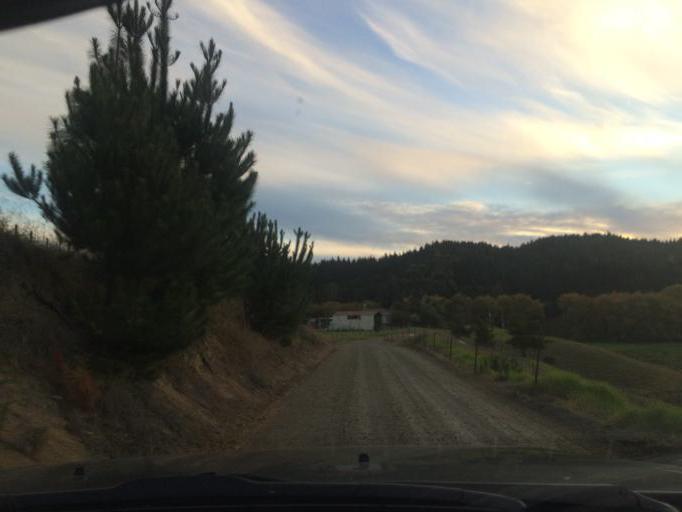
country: NZ
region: Northland
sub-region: Whangarei
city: Maungatapere
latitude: -35.8102
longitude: 174.0403
